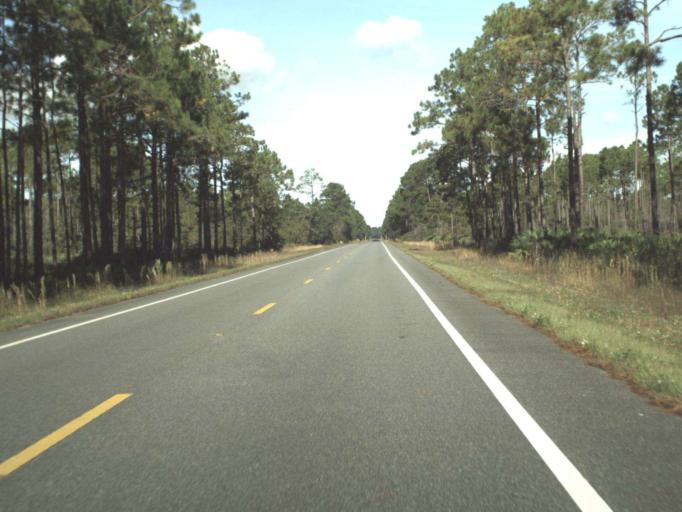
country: US
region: Florida
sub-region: Franklin County
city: Eastpoint
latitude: 29.8098
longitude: -84.8407
